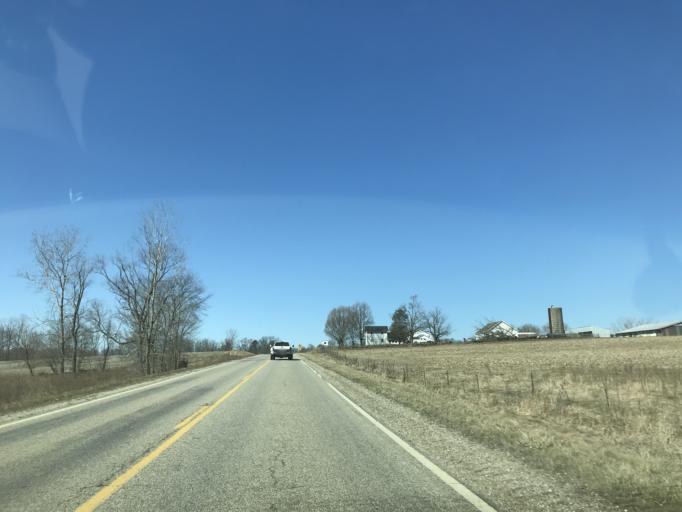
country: US
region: Michigan
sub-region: Branch County
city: Quincy
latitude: 41.9857
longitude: -84.8219
